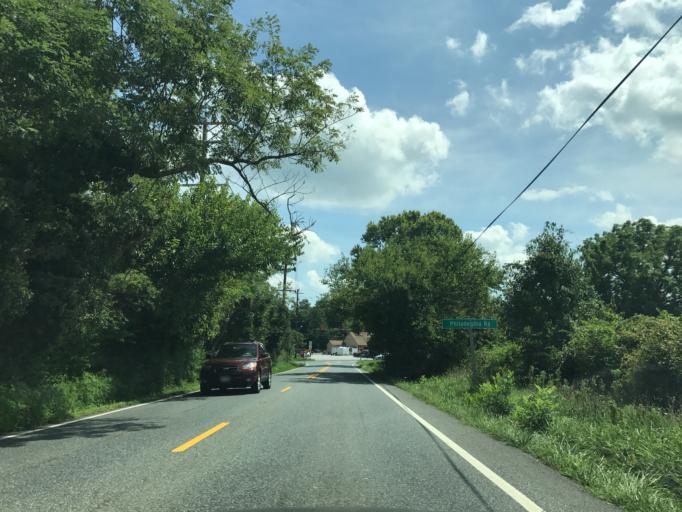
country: US
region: Maryland
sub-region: Harford County
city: Riverside
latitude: 39.4749
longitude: -76.2649
